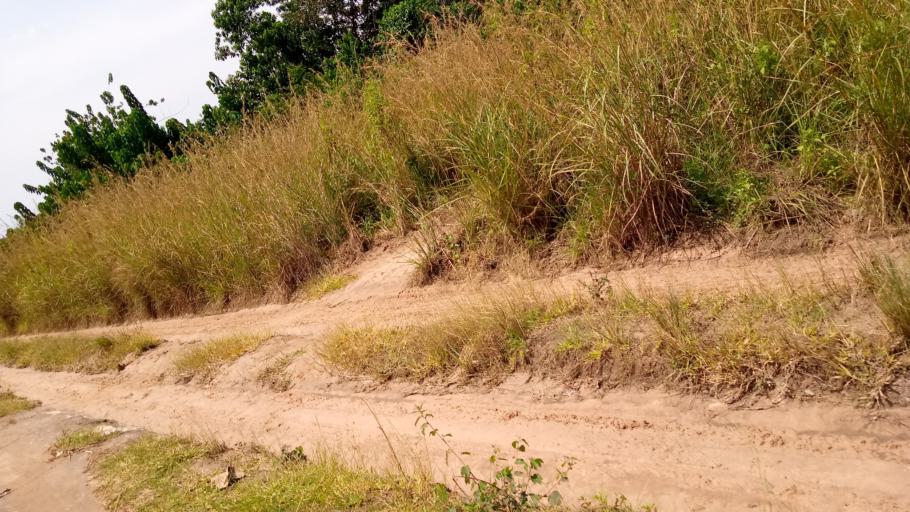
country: CD
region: Bandundu
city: Bandundu
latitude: -4.1717
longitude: 17.3956
